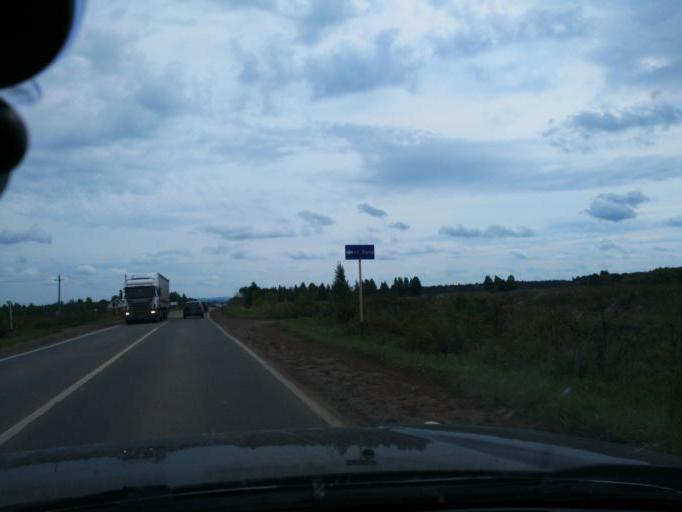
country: RU
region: Perm
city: Chernushka
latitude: 56.5085
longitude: 55.9750
